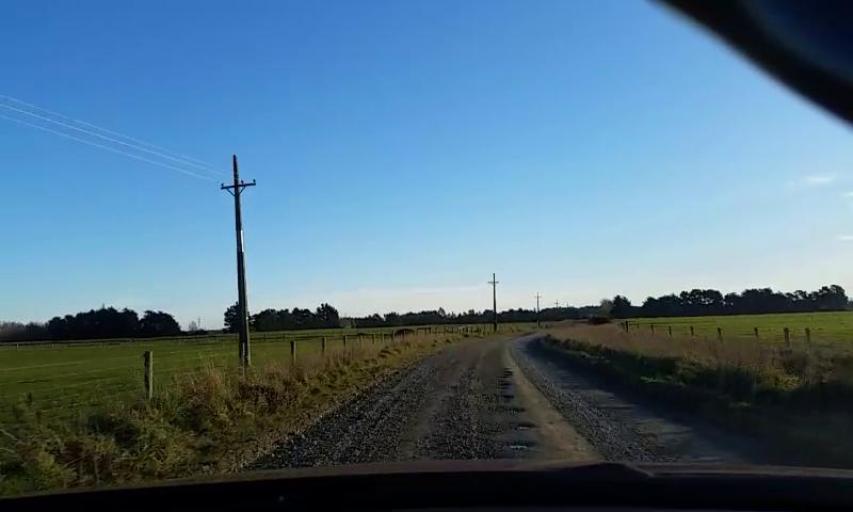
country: NZ
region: Southland
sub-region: Invercargill City
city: Invercargill
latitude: -46.2915
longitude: 168.4279
